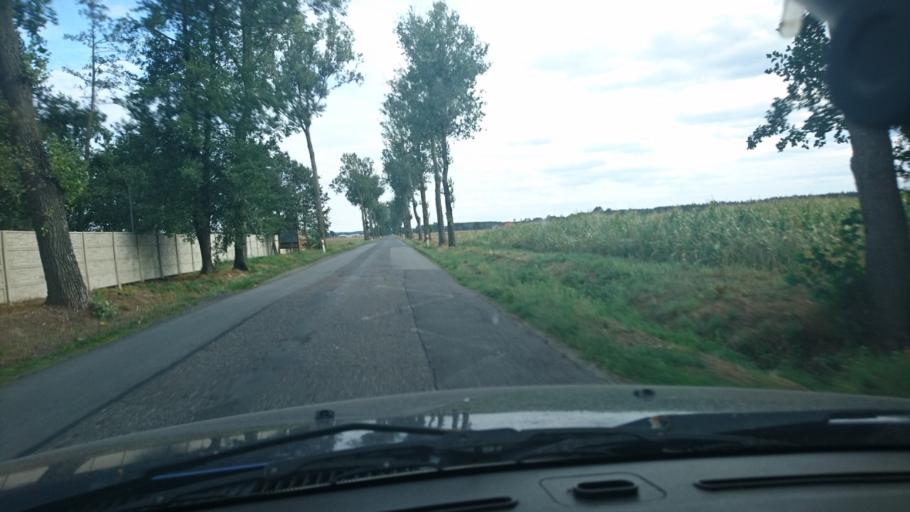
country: PL
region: Greater Poland Voivodeship
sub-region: Powiat ostrzeszowski
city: Kobyla Gora
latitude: 51.4606
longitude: 17.8129
